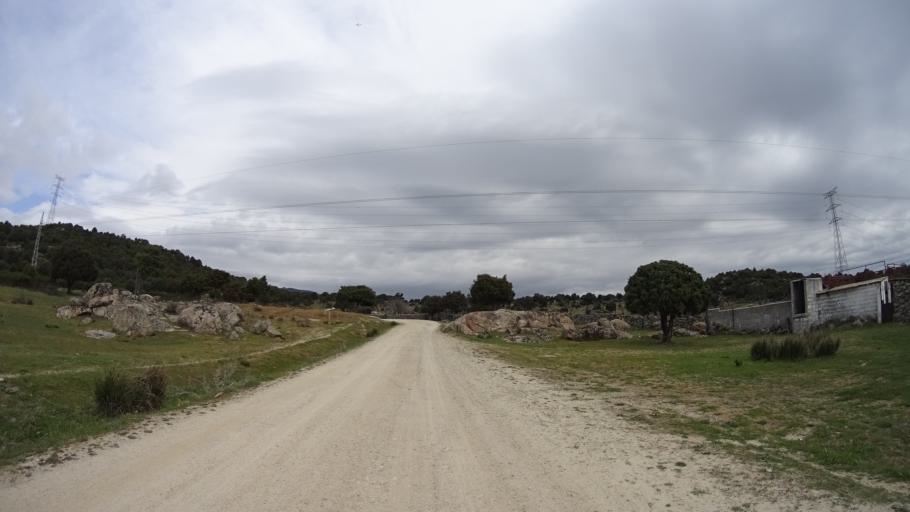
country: ES
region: Madrid
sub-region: Provincia de Madrid
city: Hoyo de Manzanares
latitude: 40.6126
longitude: -3.8784
